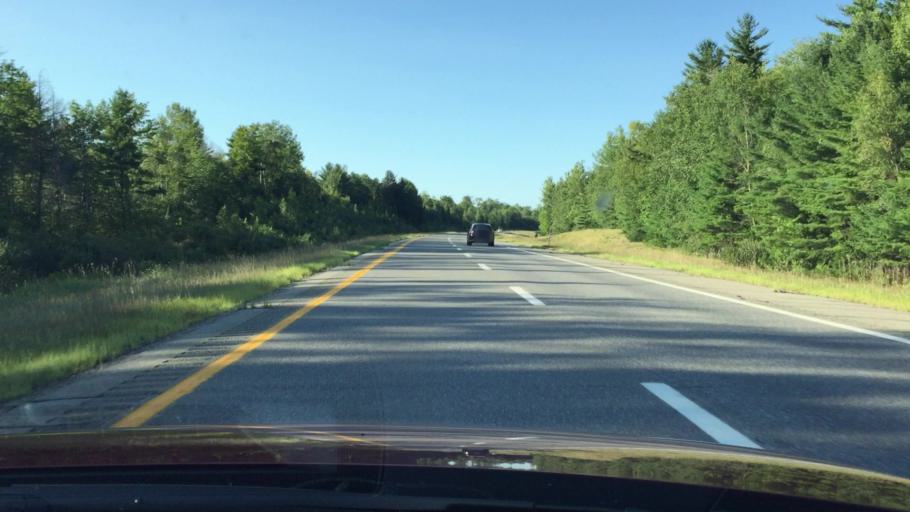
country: US
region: Maine
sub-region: Penobscot County
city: Lincoln
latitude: 45.4490
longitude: -68.5907
